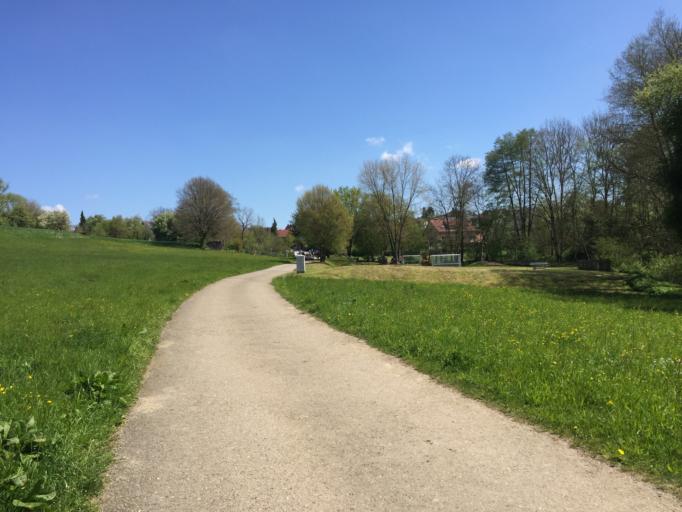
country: DE
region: Baden-Wuerttemberg
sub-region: Tuebingen Region
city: Gomaringen
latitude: 48.4775
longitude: 9.0974
